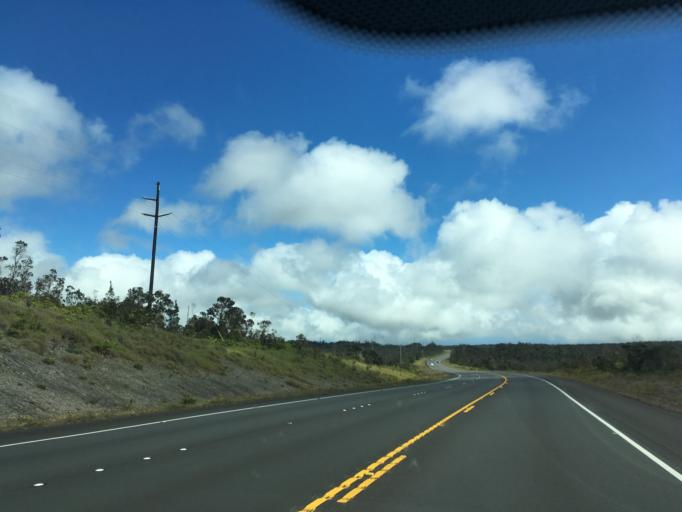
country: US
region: Hawaii
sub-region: Hawaii County
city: Wainaku
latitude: 19.6771
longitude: -155.3191
